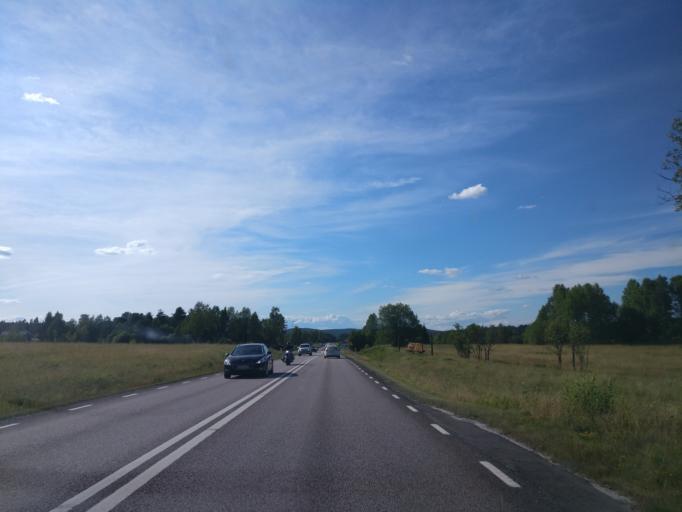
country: SE
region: Vaermland
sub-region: Karlstads Kommun
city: Edsvalla
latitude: 59.5500
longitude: 13.0564
